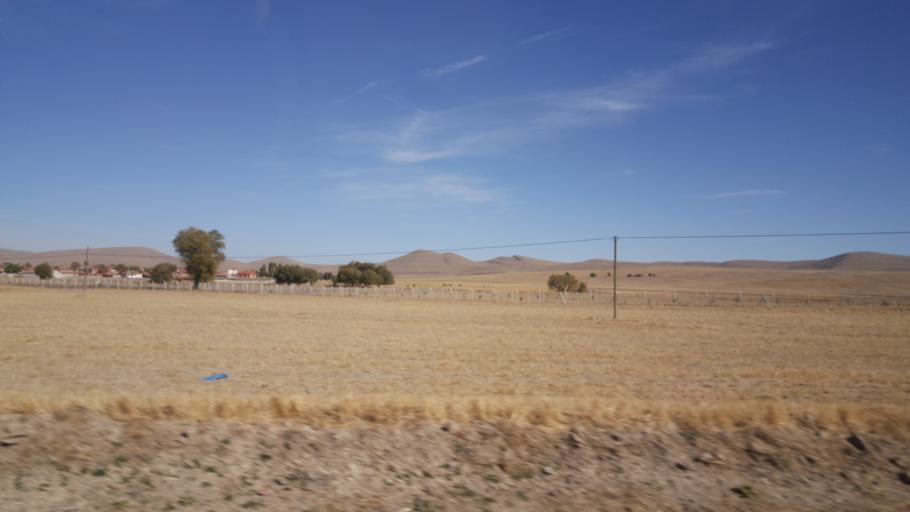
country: TR
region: Ankara
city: Altpinar
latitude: 39.2558
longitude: 32.7525
